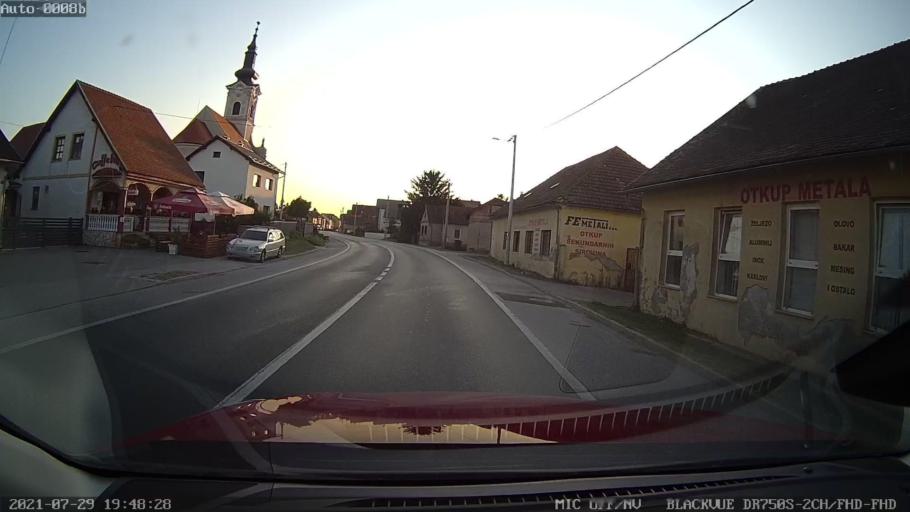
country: HR
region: Varazdinska
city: Ludbreg
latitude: 46.2645
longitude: 16.5477
